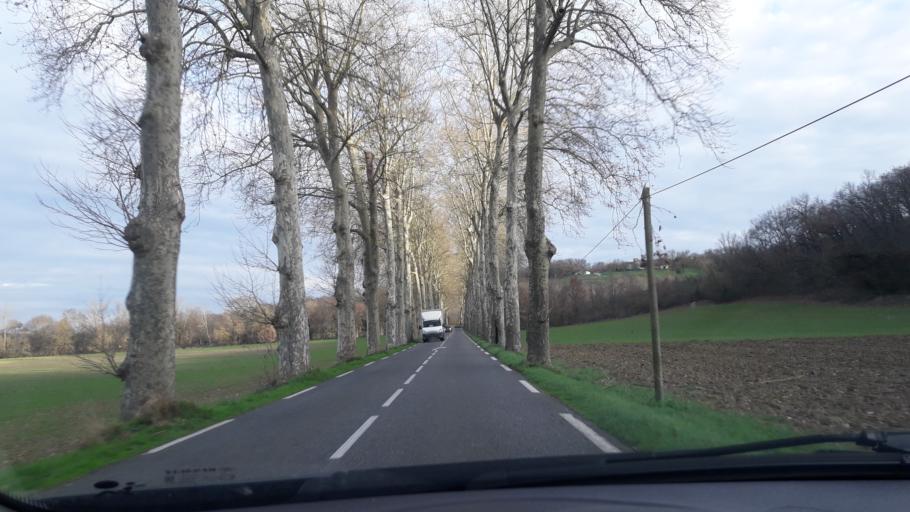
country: FR
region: Midi-Pyrenees
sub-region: Departement de la Haute-Garonne
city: Daux
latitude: 43.7163
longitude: 1.2486
